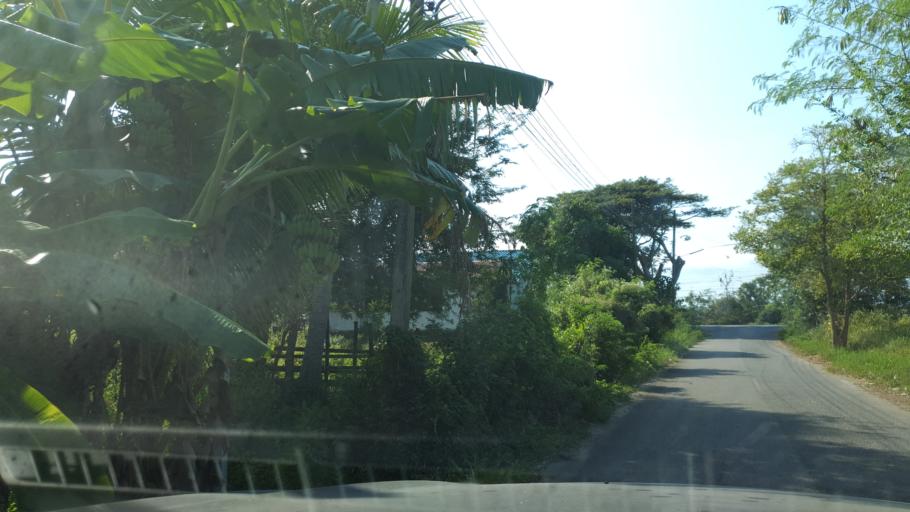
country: TH
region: Prachuap Khiri Khan
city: Thap Sakae
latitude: 11.3619
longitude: 99.5529
